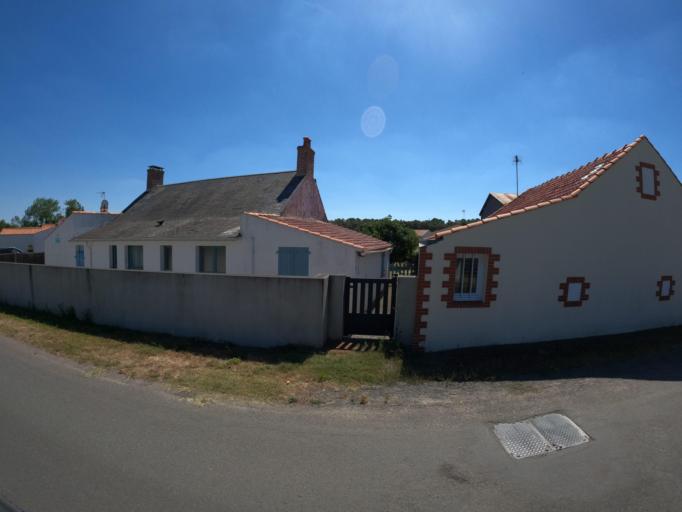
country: FR
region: Pays de la Loire
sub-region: Departement de la Vendee
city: Saint-Jean-de-Monts
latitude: 46.8035
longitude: -2.0849
